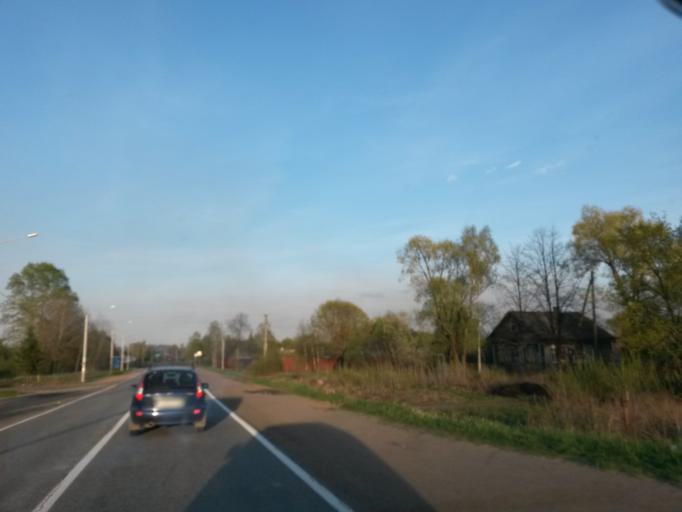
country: RU
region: Jaroslavl
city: Kurba
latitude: 57.6786
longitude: 39.5752
